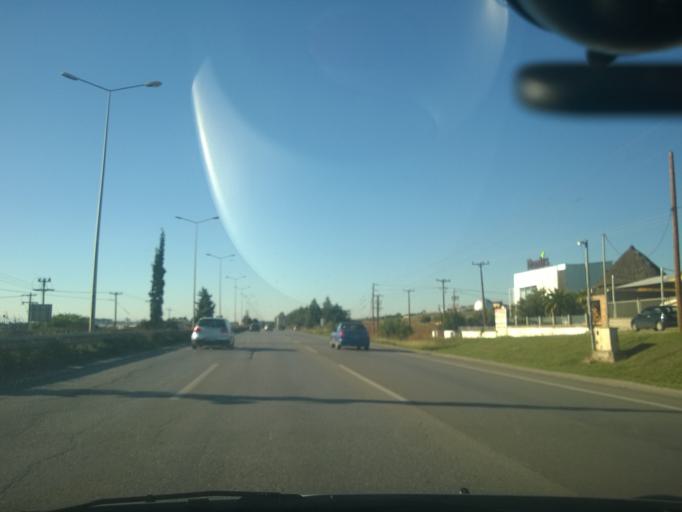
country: GR
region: Central Macedonia
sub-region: Nomos Thessalonikis
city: Thermi
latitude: 40.5554
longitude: 22.9973
